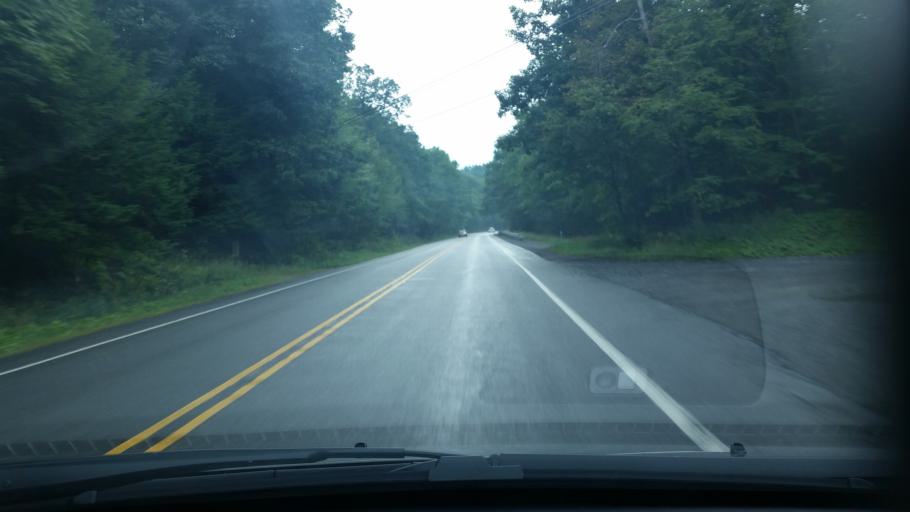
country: US
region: Pennsylvania
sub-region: Clearfield County
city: Shiloh
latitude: 41.0857
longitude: -78.2523
